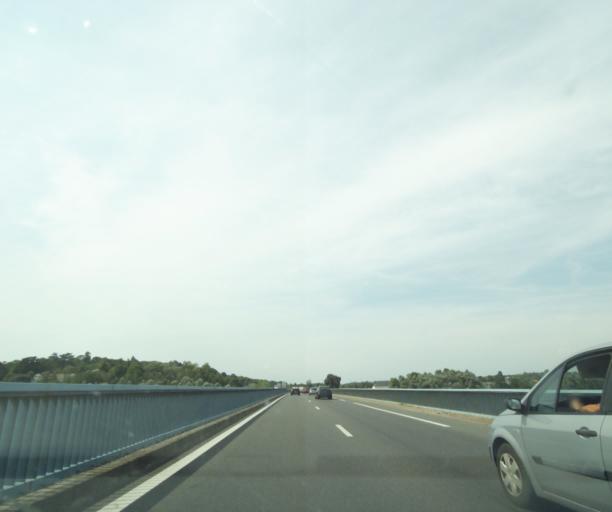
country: FR
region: Centre
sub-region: Departement d'Indre-et-Loire
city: Saint-Cyr-sur-Loire
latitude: 47.3905
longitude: 0.6483
